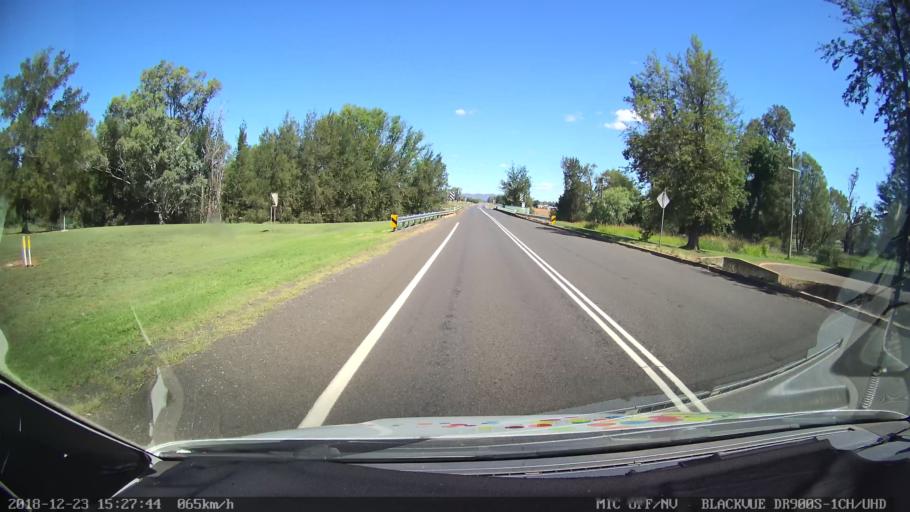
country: AU
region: New South Wales
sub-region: Tamworth Municipality
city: East Tamworth
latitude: -30.9301
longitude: 150.8473
